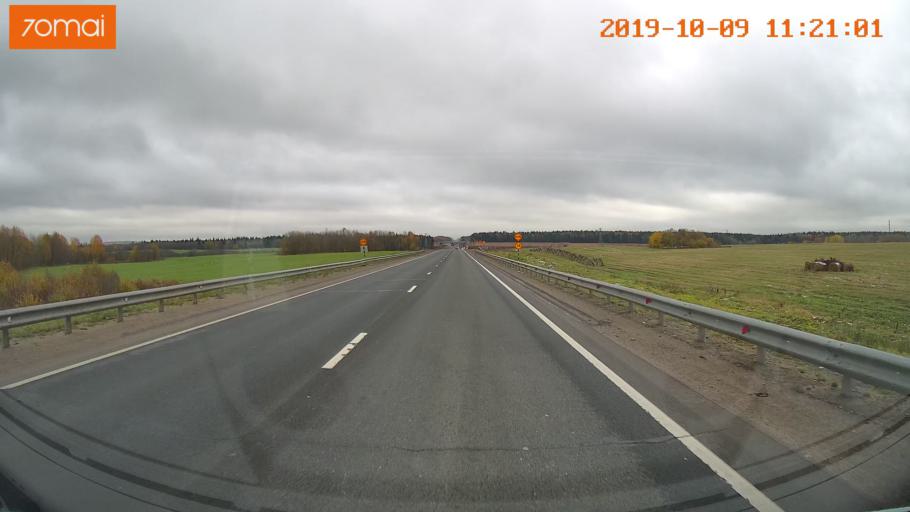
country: RU
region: Vologda
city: Vologda
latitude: 59.1431
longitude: 39.9455
